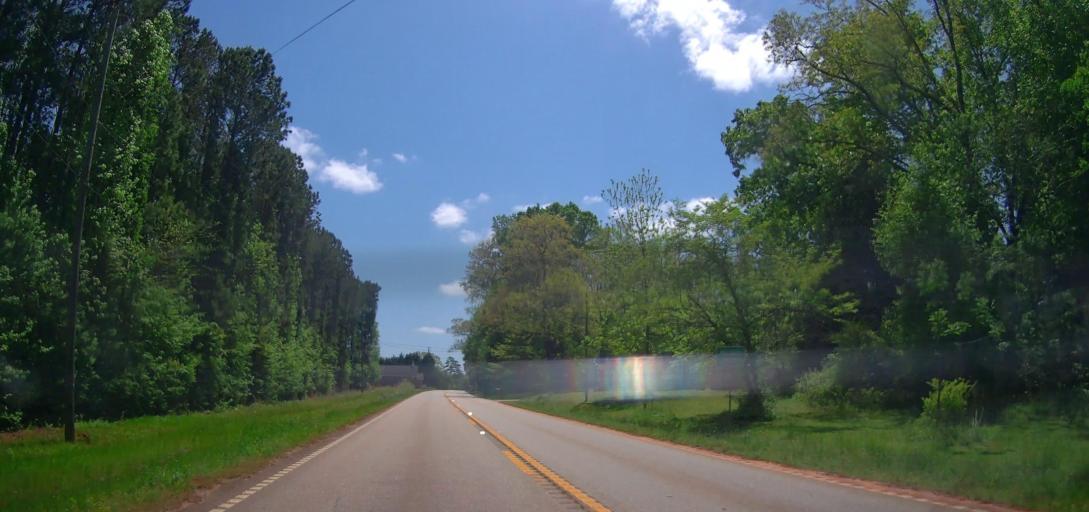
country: US
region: Georgia
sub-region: Jasper County
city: Monticello
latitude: 33.1863
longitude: -83.6453
